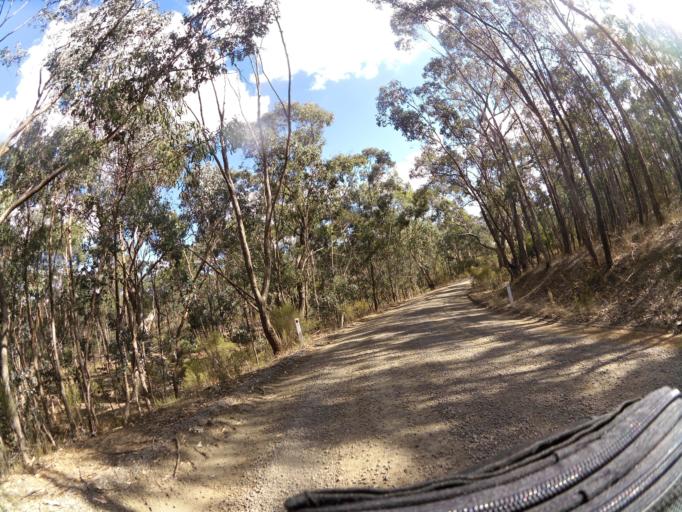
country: AU
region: Victoria
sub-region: Greater Bendigo
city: Kennington
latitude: -36.9606
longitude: 144.7792
